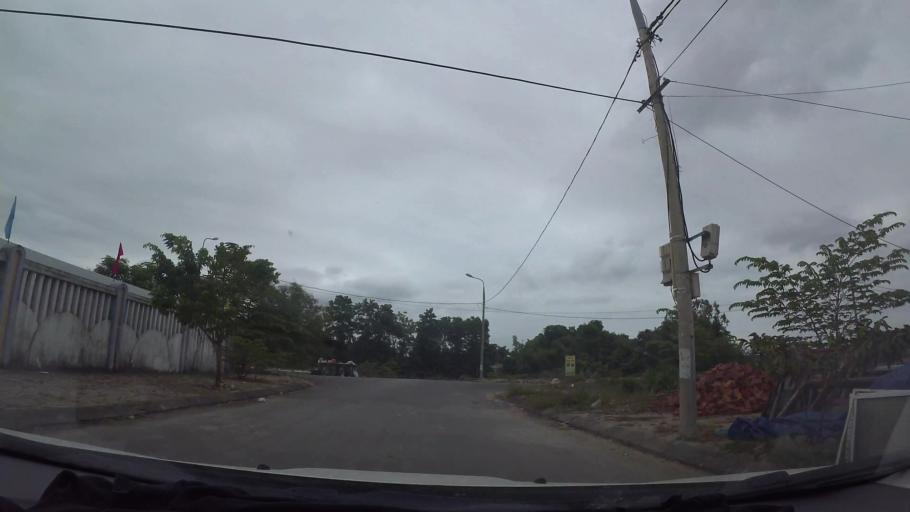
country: VN
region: Da Nang
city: Lien Chieu
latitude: 16.0958
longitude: 108.1037
